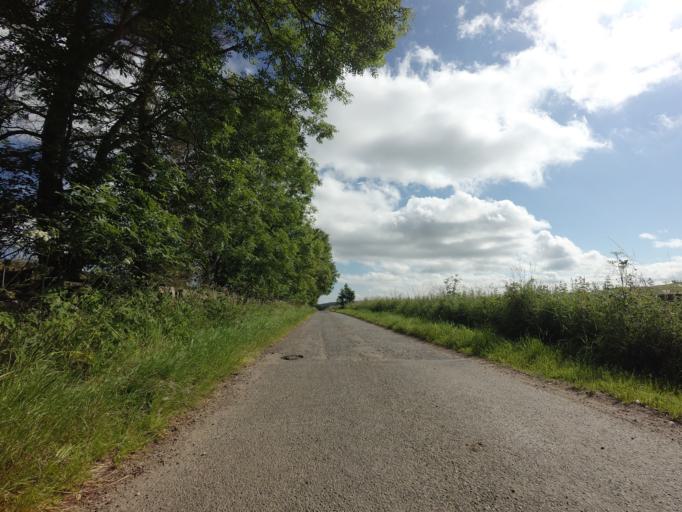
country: GB
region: Scotland
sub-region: Aberdeenshire
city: Banff
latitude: 57.6055
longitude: -2.5130
